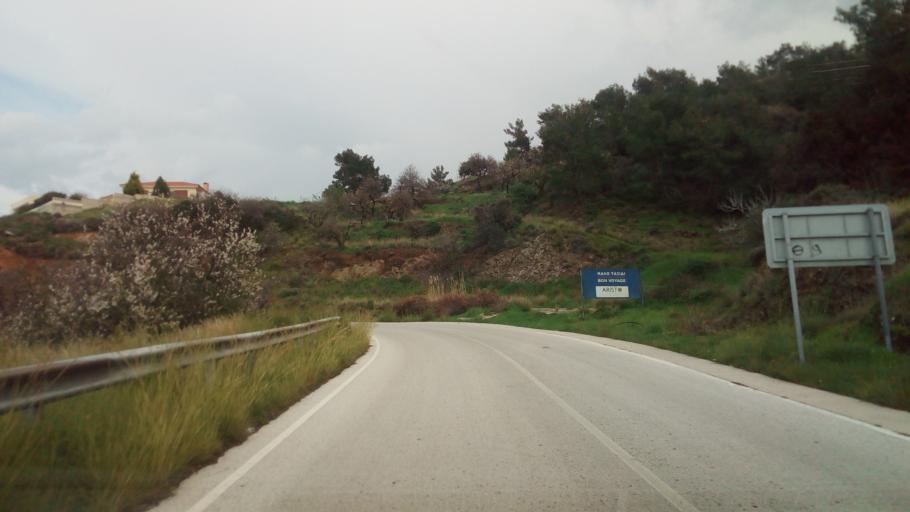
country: CY
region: Lefkosia
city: Kato Pyrgos
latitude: 35.1700
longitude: 32.5897
